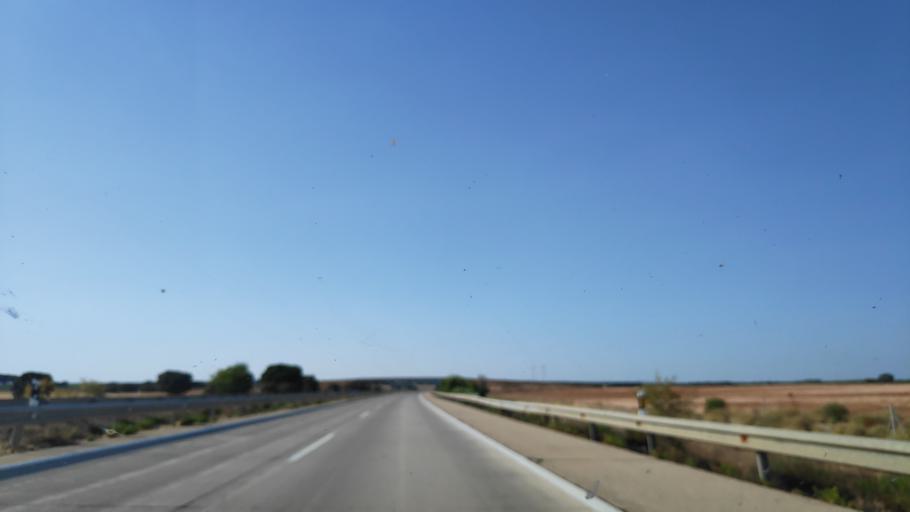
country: ES
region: Castille-La Mancha
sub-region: Provincia de Cuenca
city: Casas de Guijarro
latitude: 39.3118
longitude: -2.2032
